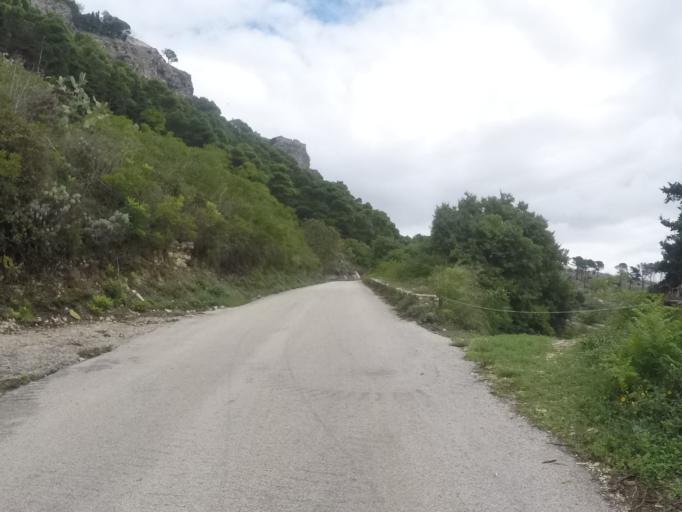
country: IT
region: Sicily
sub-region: Trapani
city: Erice
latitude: 38.0341
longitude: 12.5865
